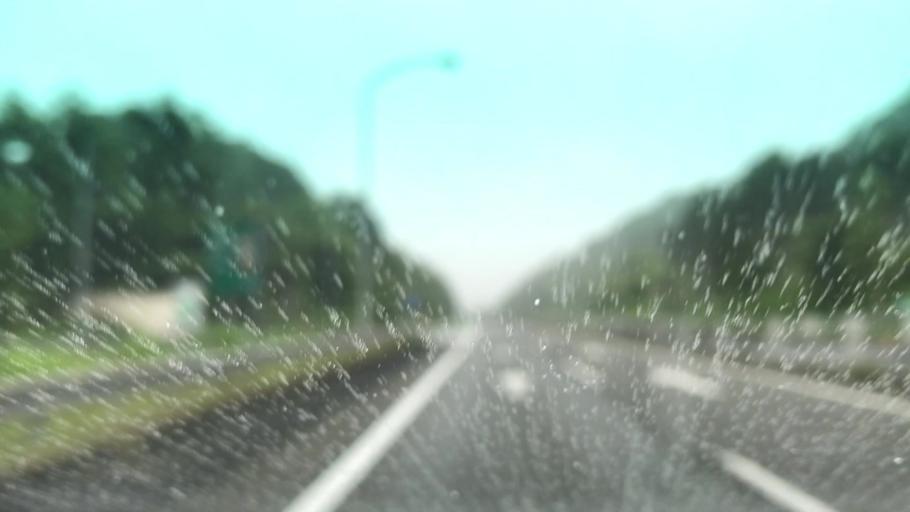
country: JP
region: Hokkaido
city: Shiraoi
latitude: 42.5429
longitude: 141.2848
